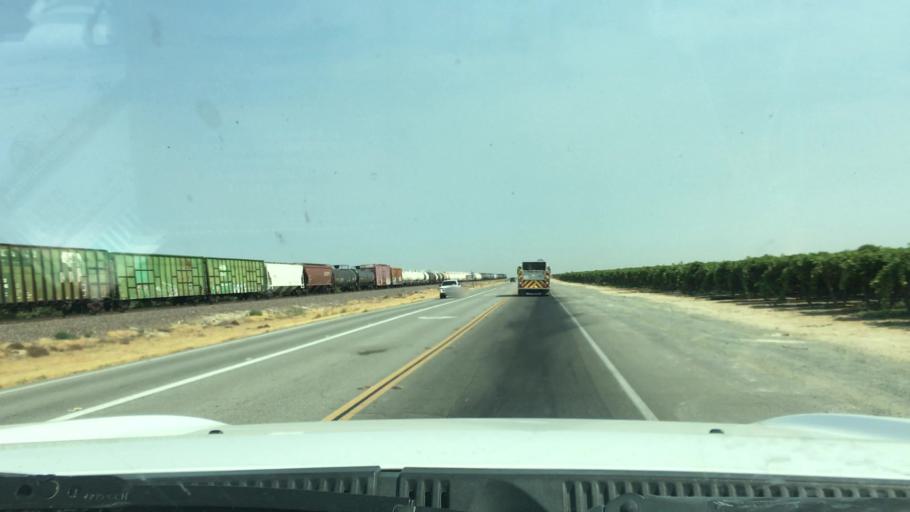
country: US
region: California
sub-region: Kern County
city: Delano
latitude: 35.7760
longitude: -119.3502
